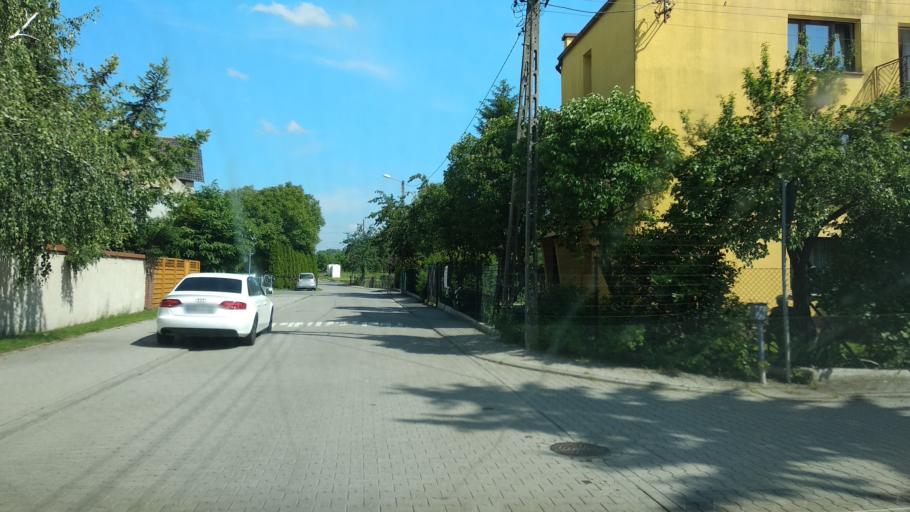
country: PL
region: Lower Silesian Voivodeship
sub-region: Powiat wroclawski
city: Zorawina
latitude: 50.9807
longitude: 17.0470
